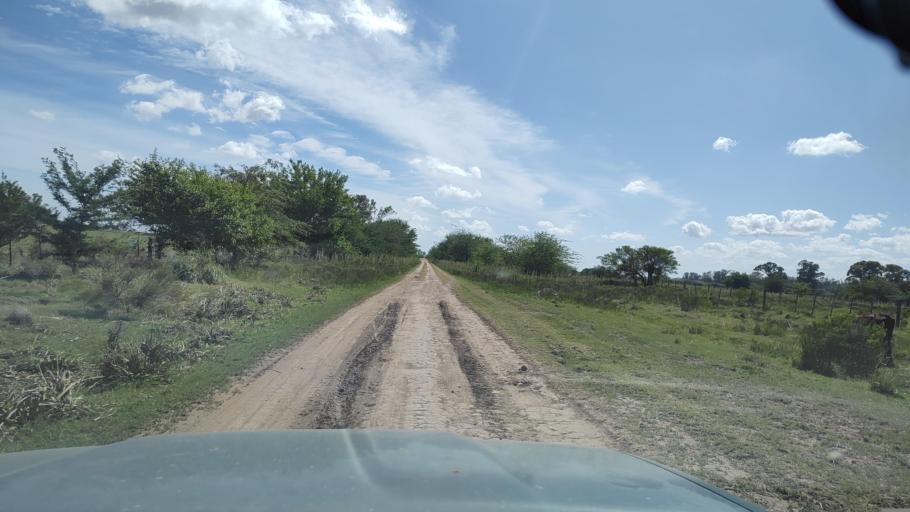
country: AR
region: Buenos Aires
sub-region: Partido de Lujan
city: Lujan
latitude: -34.5207
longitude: -59.1678
